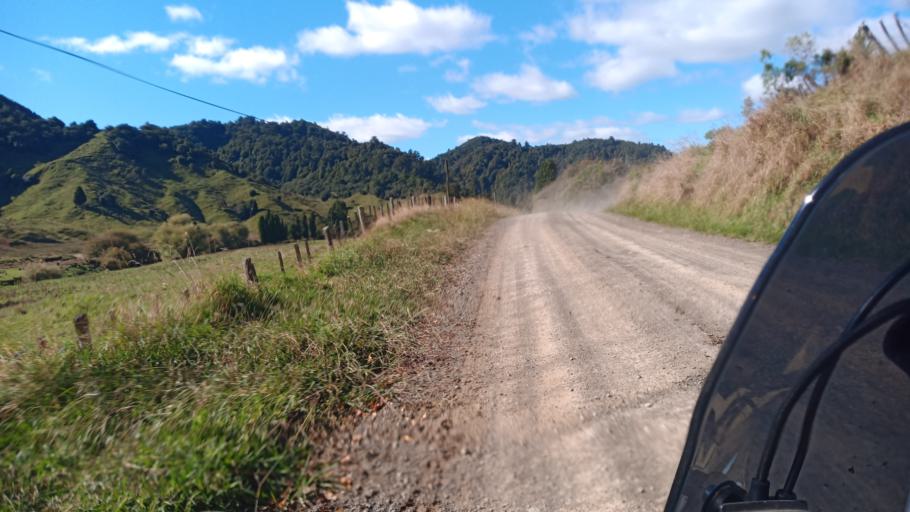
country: NZ
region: Bay of Plenty
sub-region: Opotiki District
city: Opotiki
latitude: -38.2535
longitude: 177.5802
